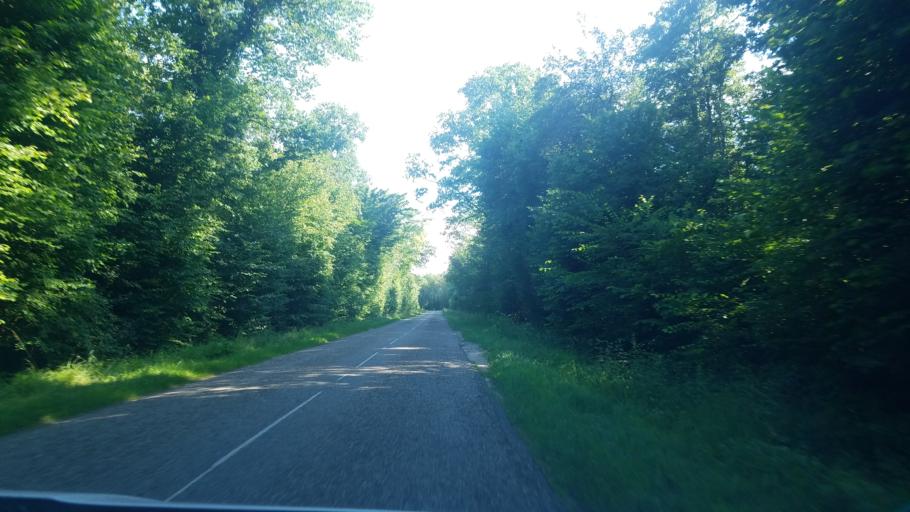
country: FR
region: Alsace
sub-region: Departement du Bas-Rhin
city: Drusenheim
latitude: 48.7933
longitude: 7.9511
